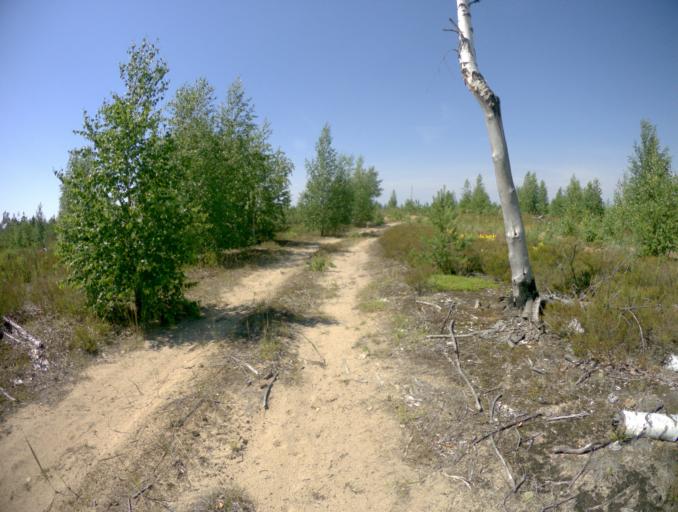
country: RU
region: Ivanovo
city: Talitsy
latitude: 56.4381
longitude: 42.2500
